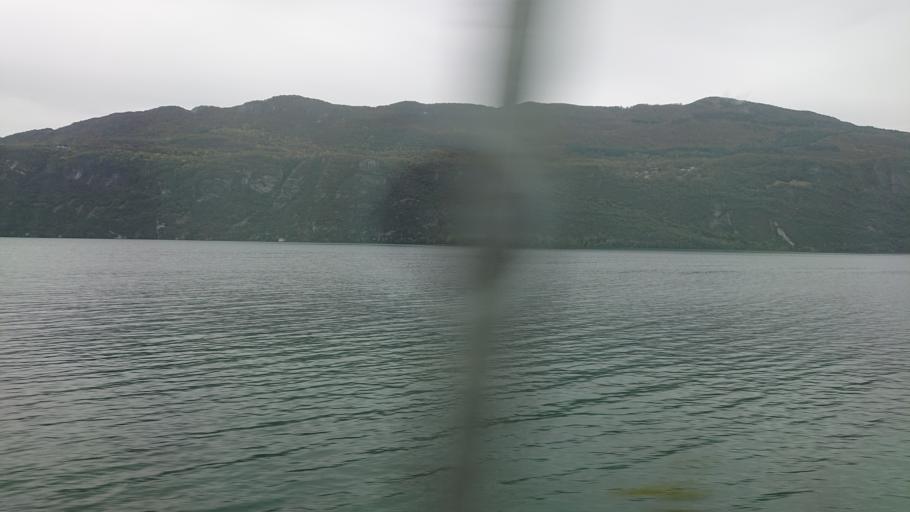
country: FR
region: Rhone-Alpes
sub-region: Departement de la Savoie
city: Brison-Saint-Innocent
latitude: 45.7306
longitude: 5.8787
